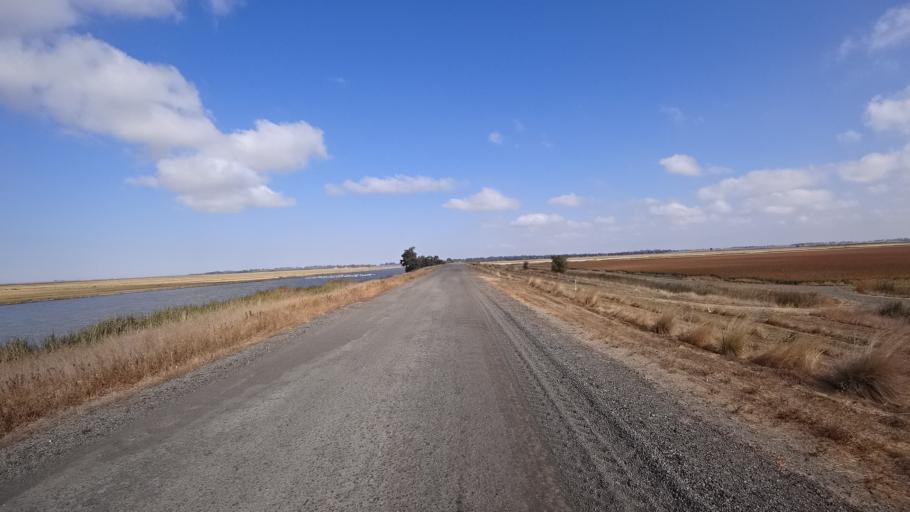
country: US
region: California
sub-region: Yolo County
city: Woodland
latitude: 38.8342
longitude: -121.7944
